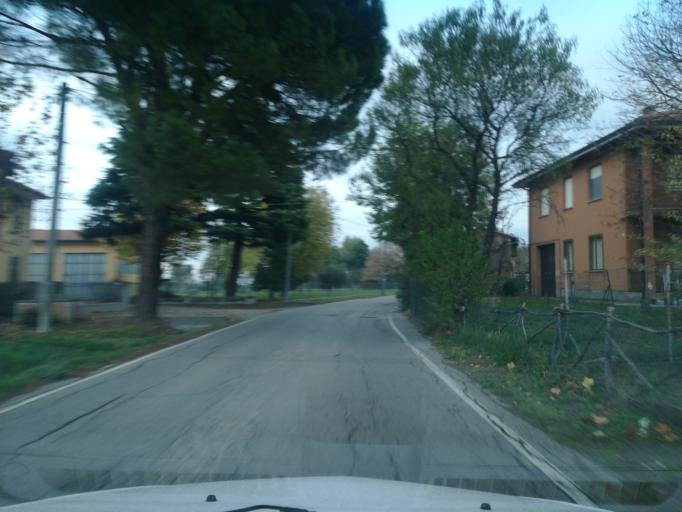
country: IT
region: Emilia-Romagna
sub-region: Provincia di Bologna
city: Imola
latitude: 44.3722
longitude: 11.7138
